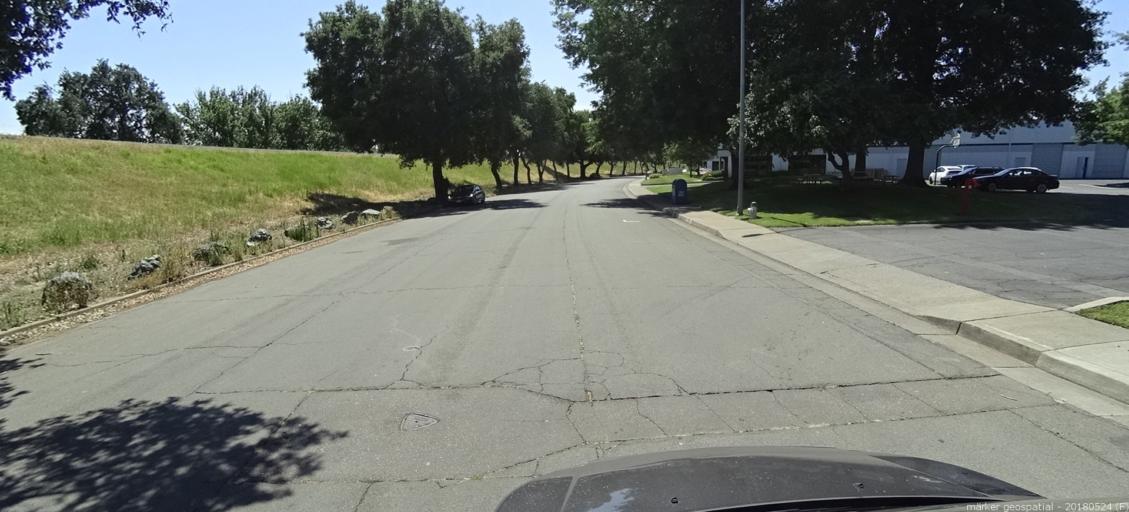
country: US
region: California
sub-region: Sacramento County
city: Sacramento
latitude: 38.5951
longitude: -121.4608
